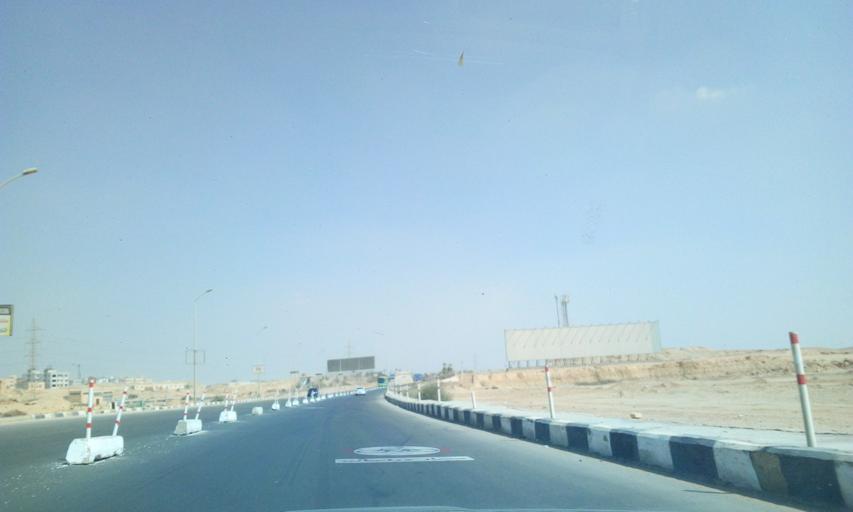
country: EG
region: Muhafazat al Qahirah
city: Halwan
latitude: 29.9664
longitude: 31.4720
